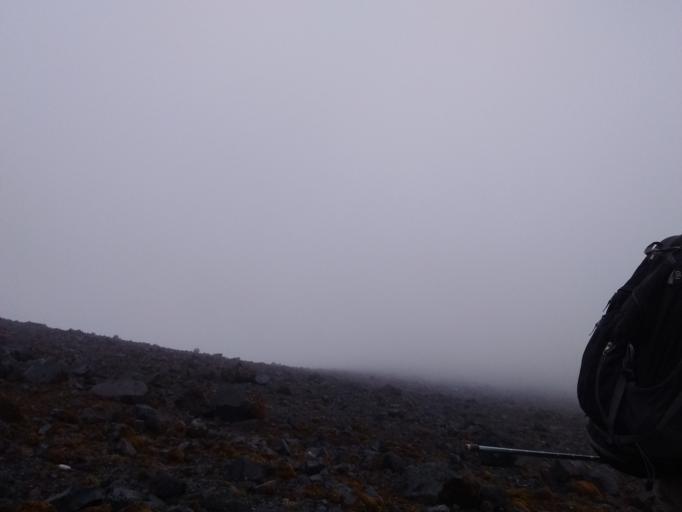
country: CO
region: Cauca
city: Totoro
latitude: 2.3194
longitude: -76.3942
